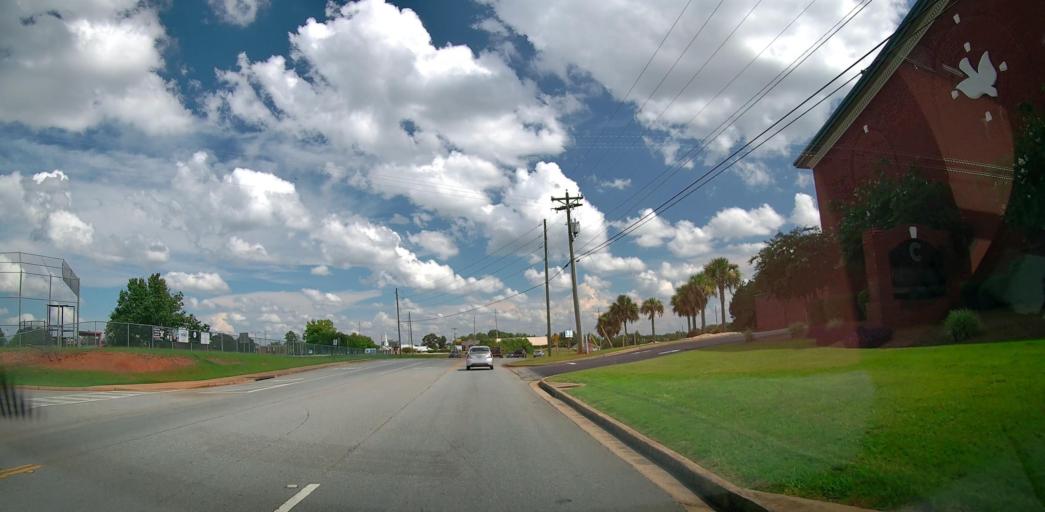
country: US
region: Georgia
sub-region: Houston County
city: Centerville
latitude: 32.5964
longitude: -83.6566
